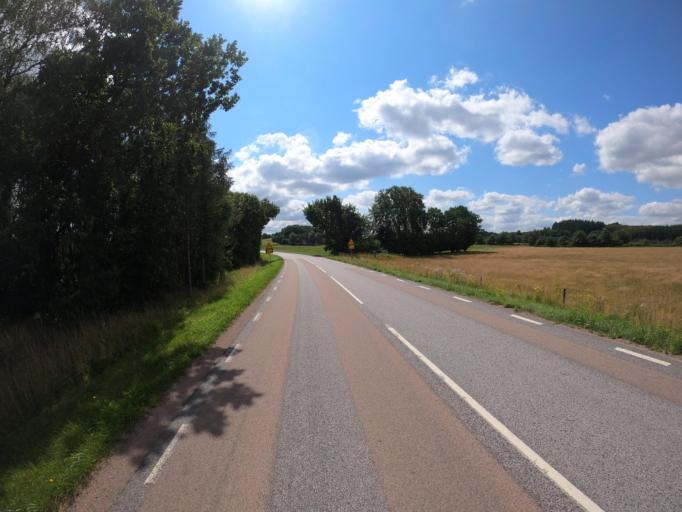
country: SE
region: Skane
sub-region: Lunds Kommun
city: Veberod
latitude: 55.6085
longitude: 13.4879
